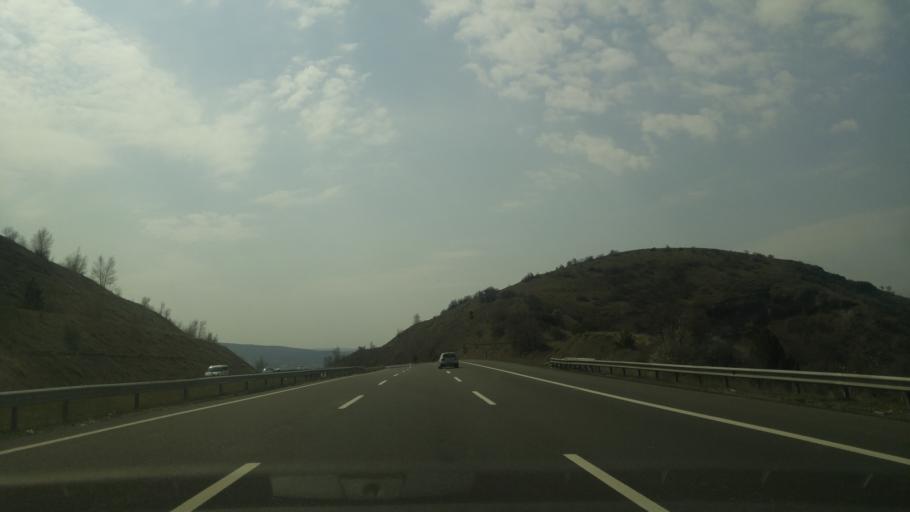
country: TR
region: Ankara
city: Celtikci
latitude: 40.3560
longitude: 32.4690
